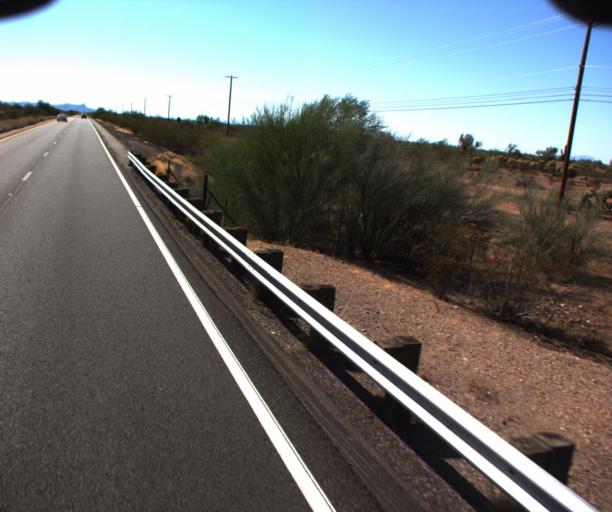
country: US
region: Arizona
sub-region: Pinal County
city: Gold Camp
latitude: 33.3207
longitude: -111.4238
